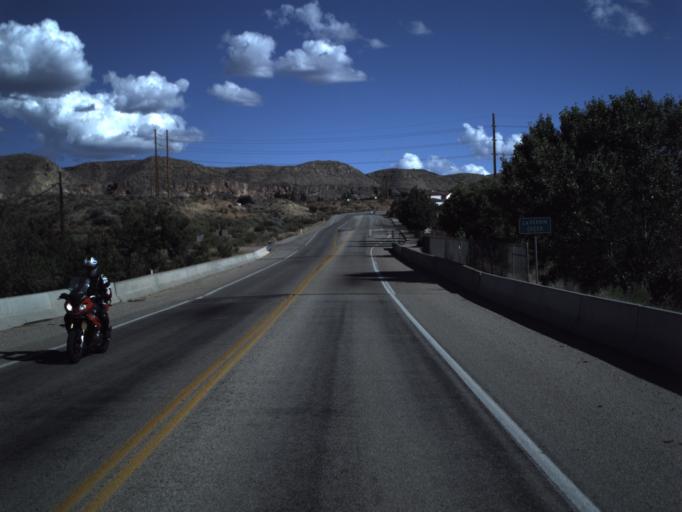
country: US
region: Utah
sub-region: Washington County
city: LaVerkin
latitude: 37.2198
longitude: -113.2763
